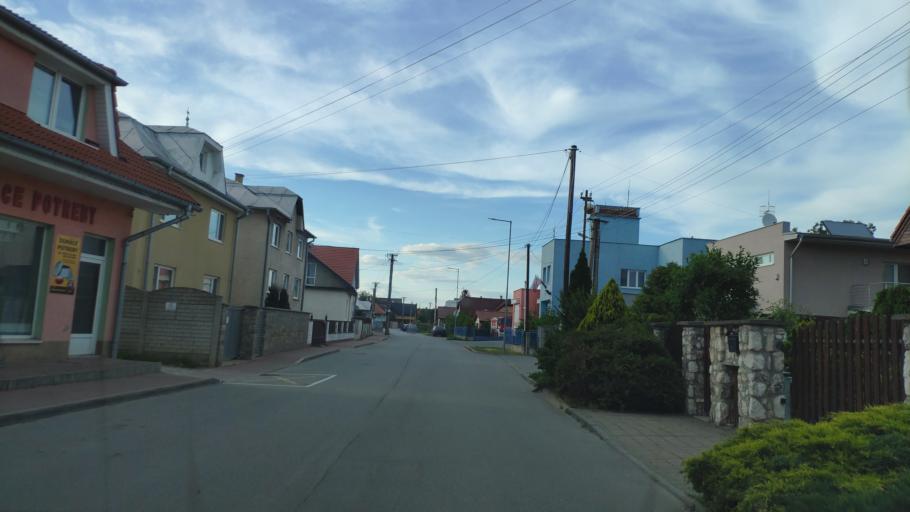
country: SK
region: Kosicky
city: Kosice
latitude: 48.6082
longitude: 21.3259
